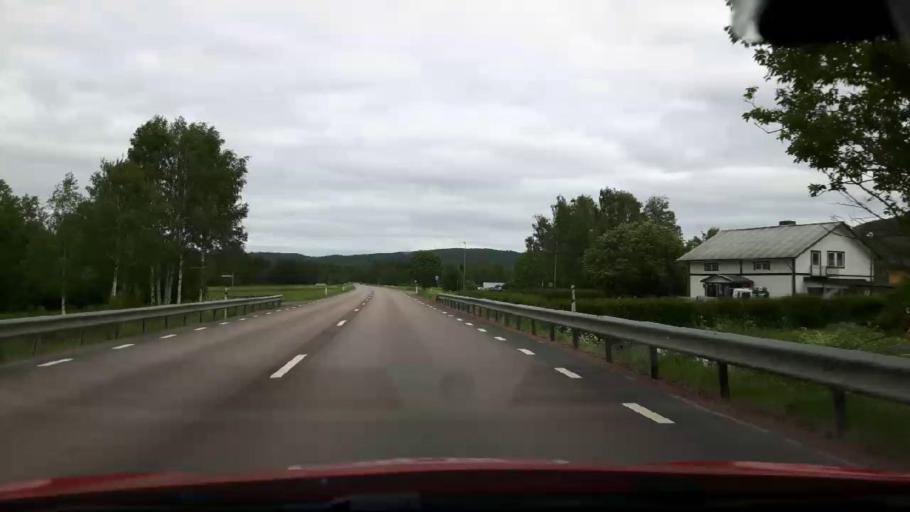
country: SE
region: Jaemtland
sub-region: Ragunda Kommun
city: Hammarstrand
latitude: 63.1500
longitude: 16.2686
